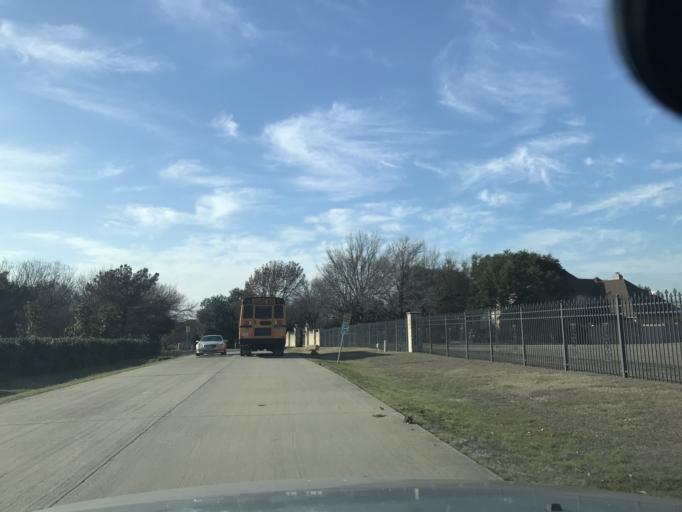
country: US
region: Texas
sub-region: Denton County
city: The Colony
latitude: 33.0975
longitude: -96.8336
